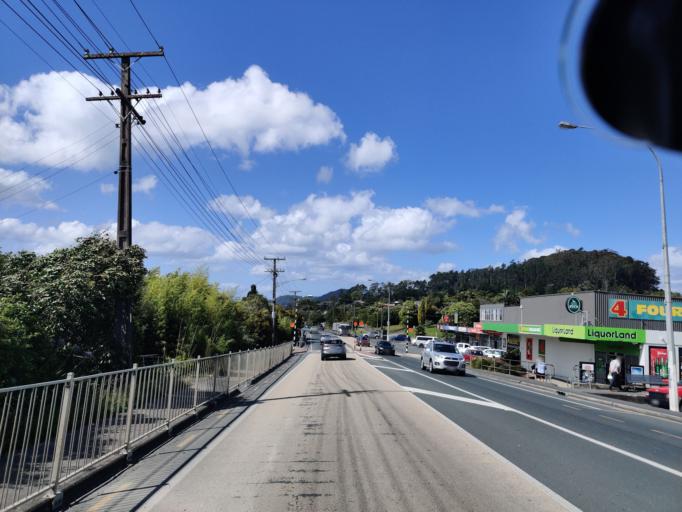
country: NZ
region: Northland
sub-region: Whangarei
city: Whangarei
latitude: -35.7434
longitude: 174.3071
